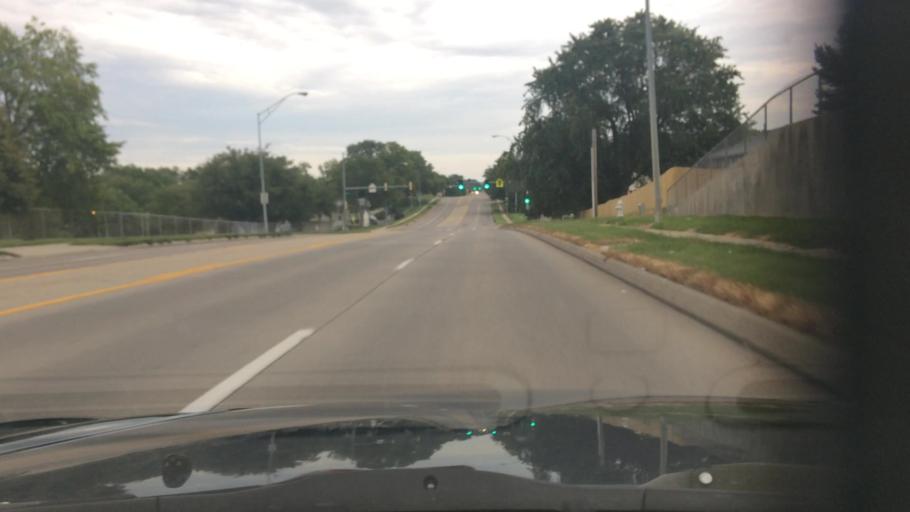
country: US
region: Nebraska
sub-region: Douglas County
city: Ralston
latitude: 41.2053
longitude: -96.0578
